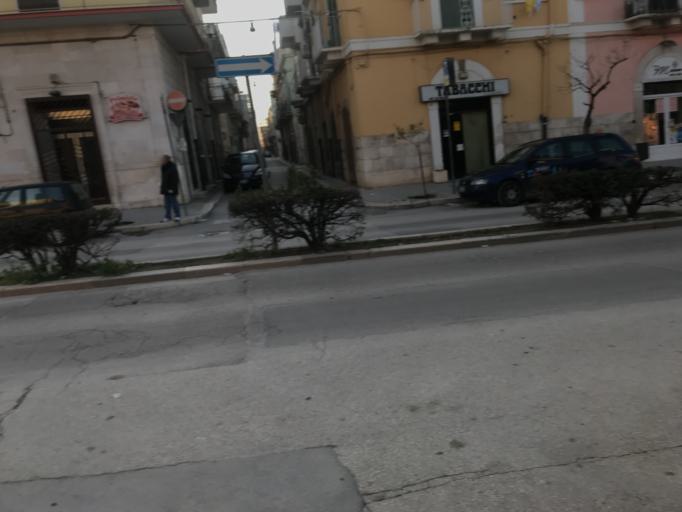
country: IT
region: Apulia
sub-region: Provincia di Bari
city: Corato
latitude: 41.1510
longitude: 16.4163
